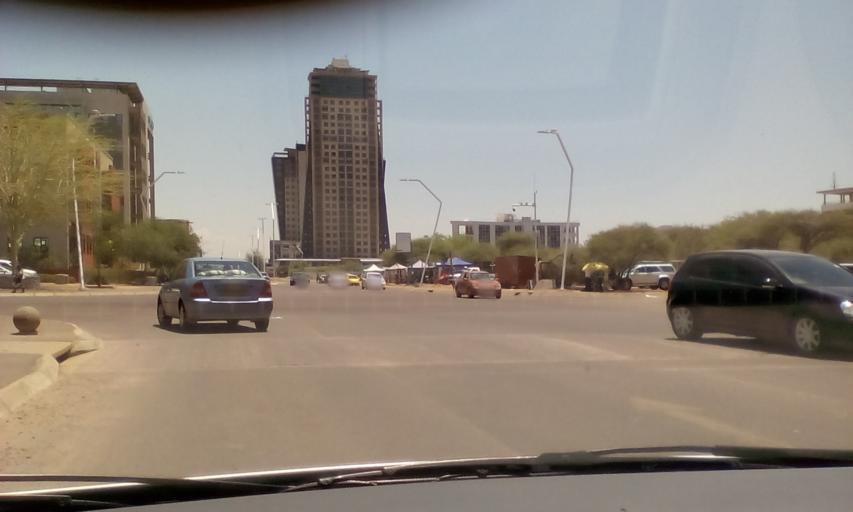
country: BW
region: South East
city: Gaborone
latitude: -24.6522
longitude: 25.9035
